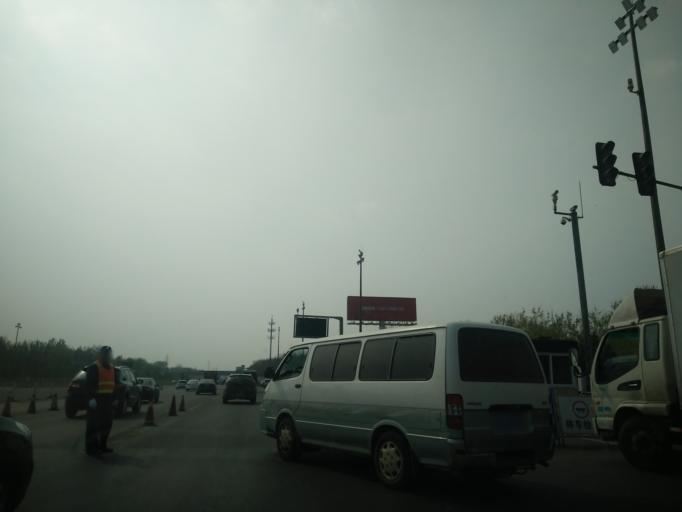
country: CN
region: Beijing
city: Taihu
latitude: 39.8670
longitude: 116.5728
